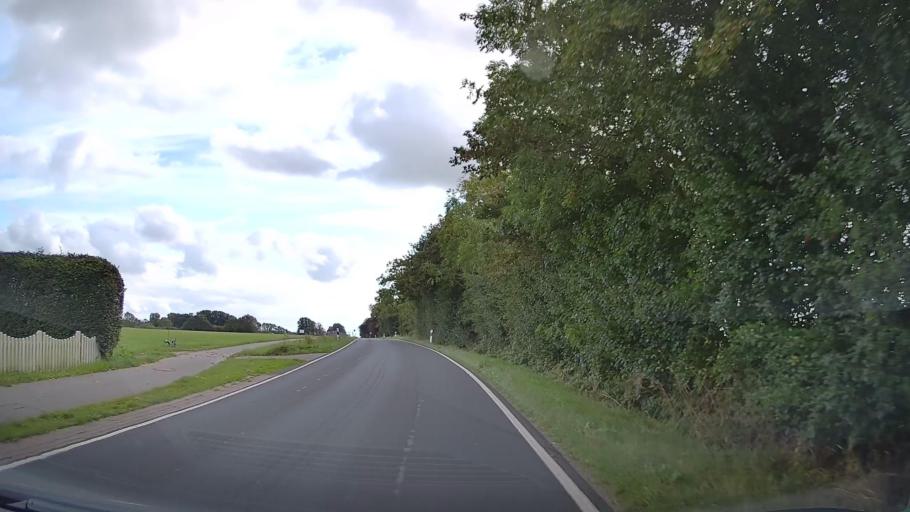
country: DE
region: Schleswig-Holstein
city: Steinberg
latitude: 54.7605
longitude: 9.7995
